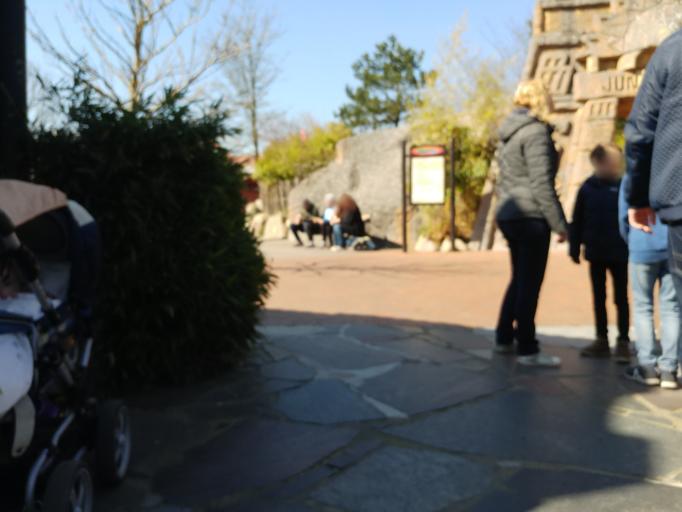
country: DK
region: South Denmark
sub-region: Billund Kommune
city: Billund
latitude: 55.7369
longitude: 9.1234
